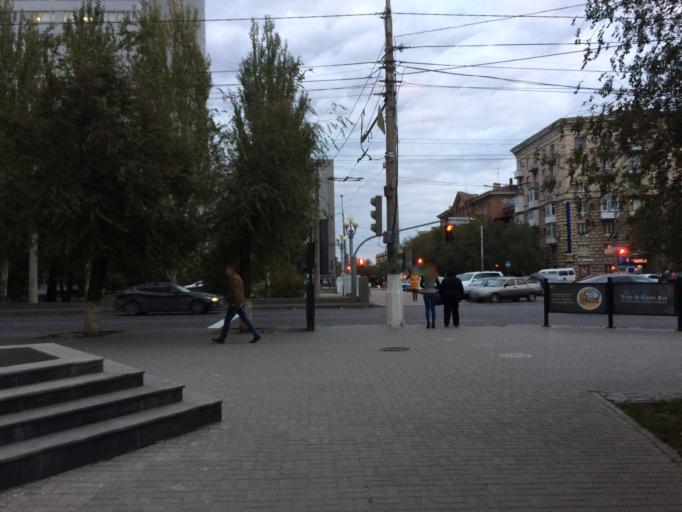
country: RU
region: Volgograd
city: Volgograd
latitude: 48.7131
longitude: 44.5254
